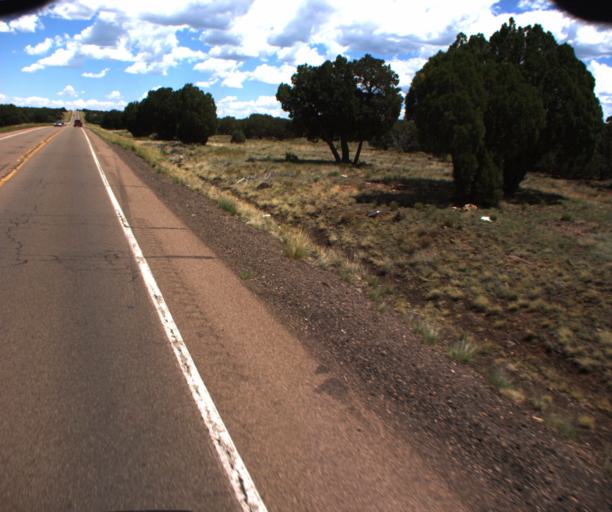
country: US
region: Arizona
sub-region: Navajo County
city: Show Low
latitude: 34.2626
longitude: -109.9778
